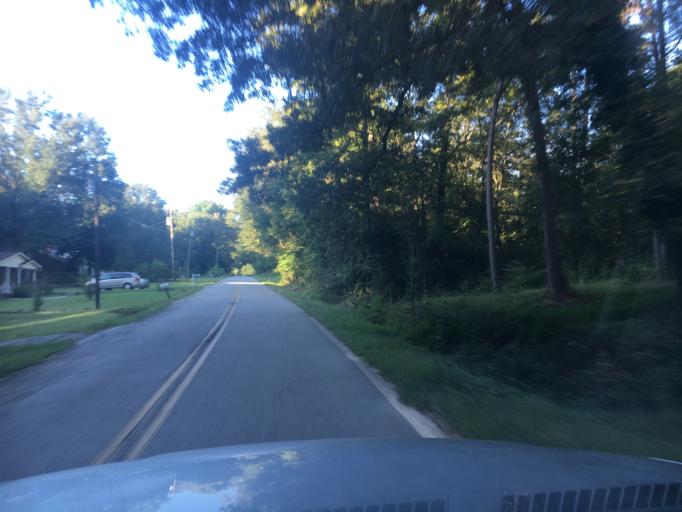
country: US
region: South Carolina
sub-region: Spartanburg County
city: Woodruff
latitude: 34.6653
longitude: -81.9650
